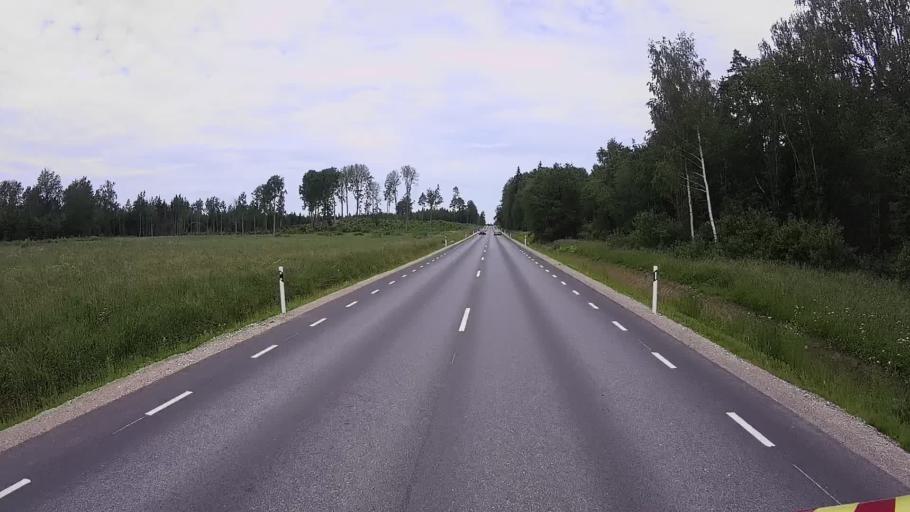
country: EE
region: Viljandimaa
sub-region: Viljandi linn
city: Viljandi
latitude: 58.2534
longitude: 25.5901
